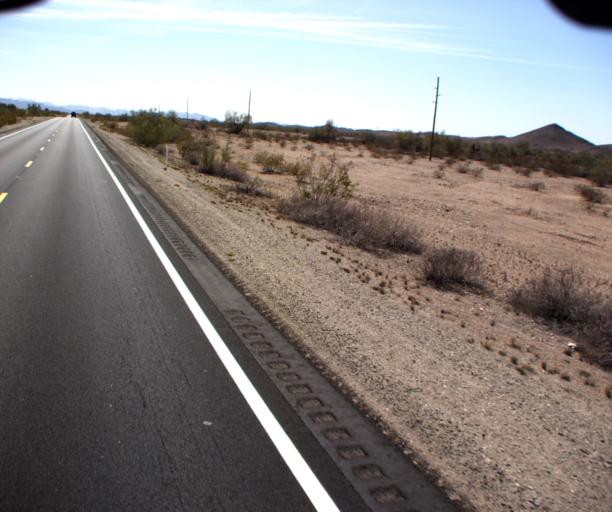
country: US
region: Arizona
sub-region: Yuma County
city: Wellton
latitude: 32.9887
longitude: -114.2879
